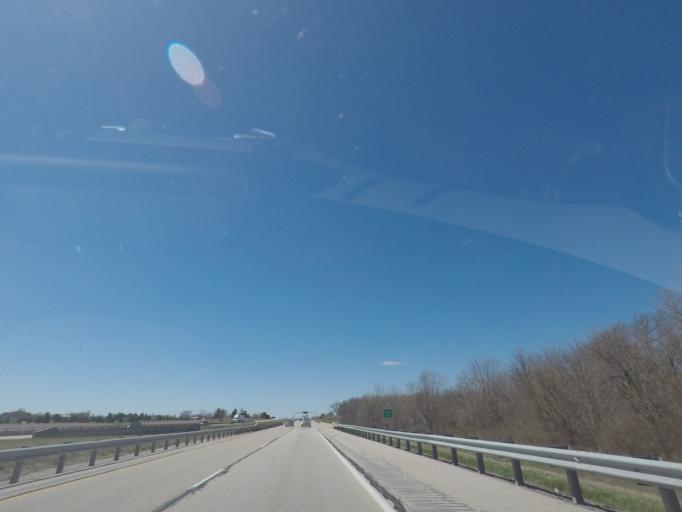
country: US
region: Illinois
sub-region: McLean County
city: Hudson
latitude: 40.5830
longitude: -88.8825
